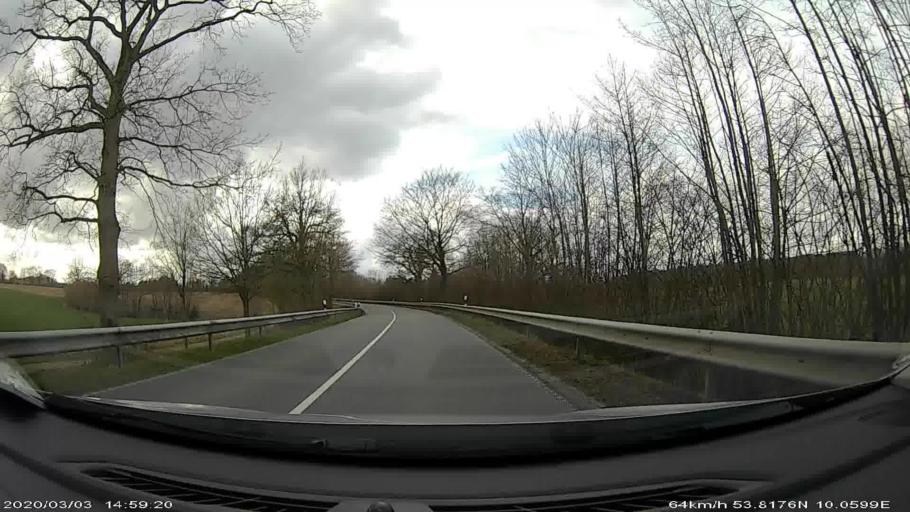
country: DE
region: Schleswig-Holstein
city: Huttblek
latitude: 53.8176
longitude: 10.0605
